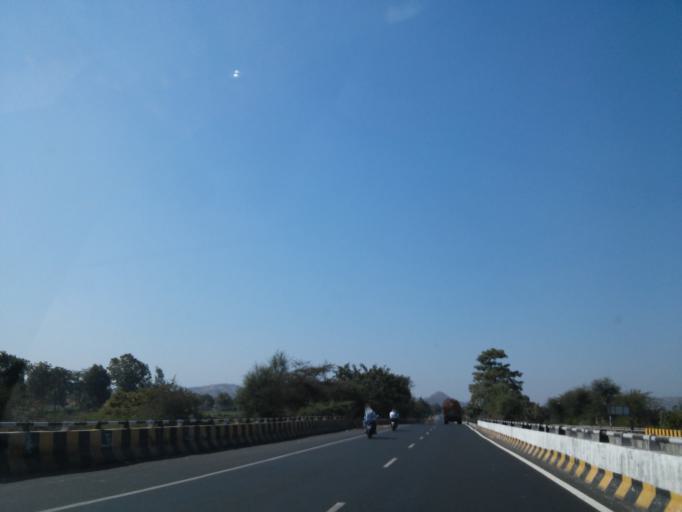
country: IN
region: Gujarat
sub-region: Sabar Kantha
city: Modasa
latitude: 23.6219
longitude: 73.2901
